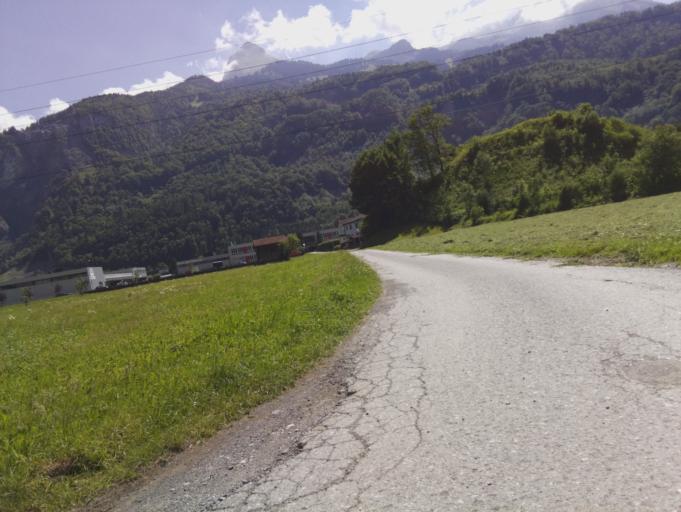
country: CH
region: Glarus
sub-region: Glarus
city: Netstal
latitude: 47.0703
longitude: 9.0539
